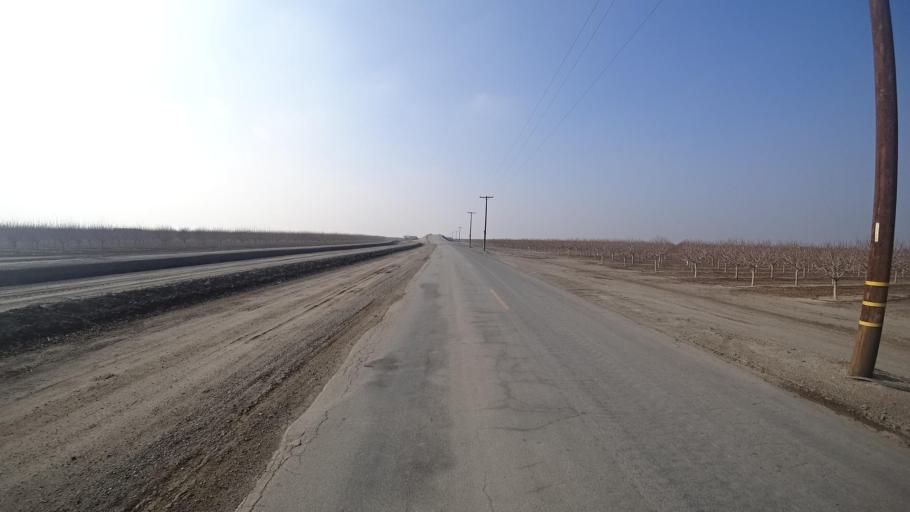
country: US
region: California
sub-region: Kern County
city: Greenfield
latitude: 35.1517
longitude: -119.0948
